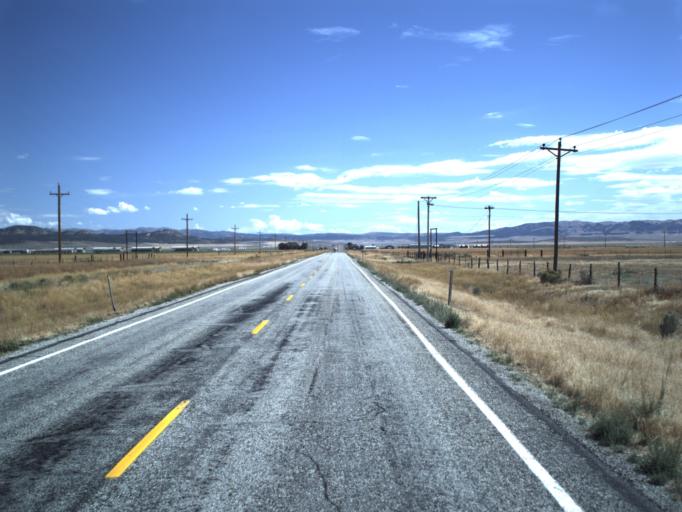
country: US
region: Idaho
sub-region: Oneida County
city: Malad City
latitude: 41.9664
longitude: -112.9233
